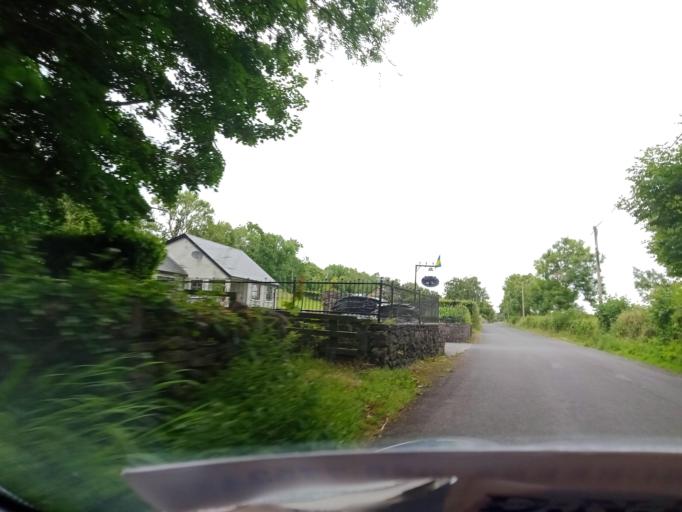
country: IE
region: Leinster
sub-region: Kilkenny
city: Thomastown
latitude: 52.5819
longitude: -7.1868
